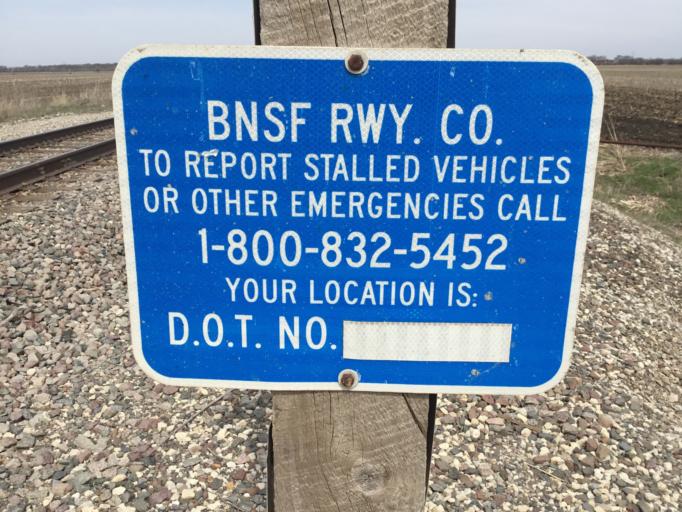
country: US
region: Kansas
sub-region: Butler County
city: Douglass
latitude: 37.5596
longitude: -97.0005
